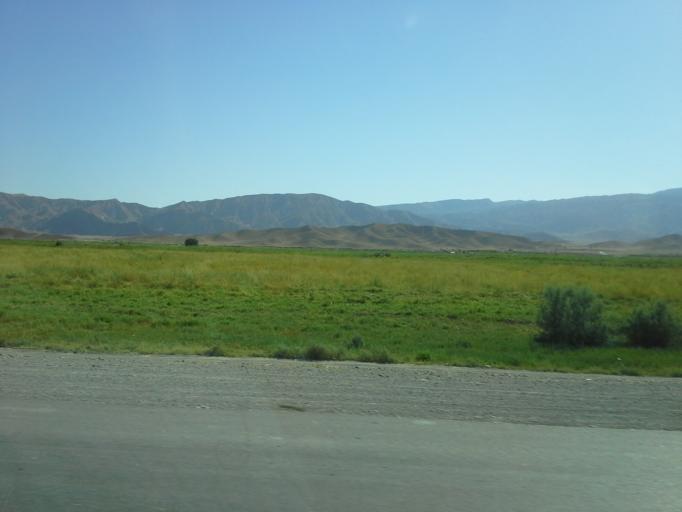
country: TM
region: Ahal
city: Baharly
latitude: 38.3490
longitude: 57.5508
